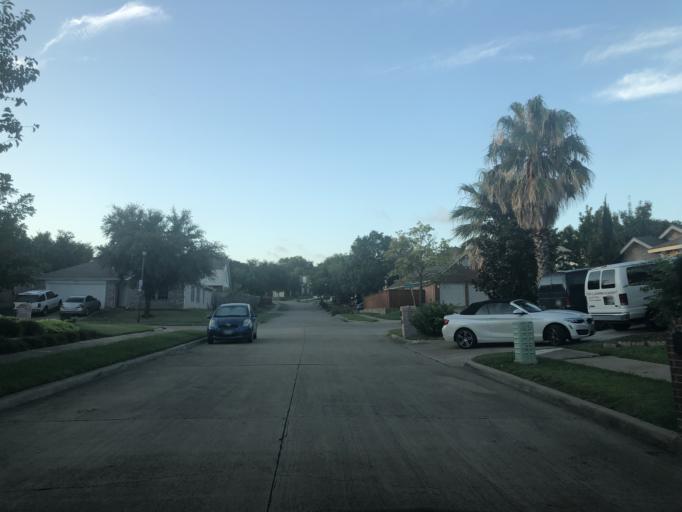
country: US
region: Texas
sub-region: Dallas County
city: Duncanville
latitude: 32.6514
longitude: -96.9711
